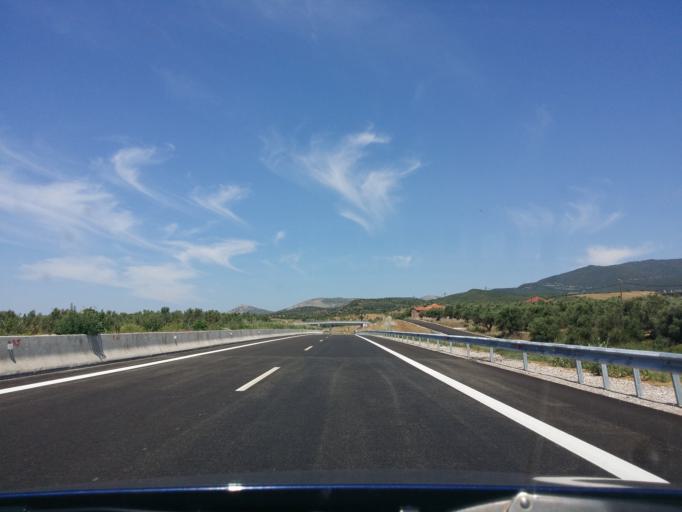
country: GR
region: West Greece
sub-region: Nomos Aitolias kai Akarnanias
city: Mesolongi
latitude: 38.3892
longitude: 21.4801
